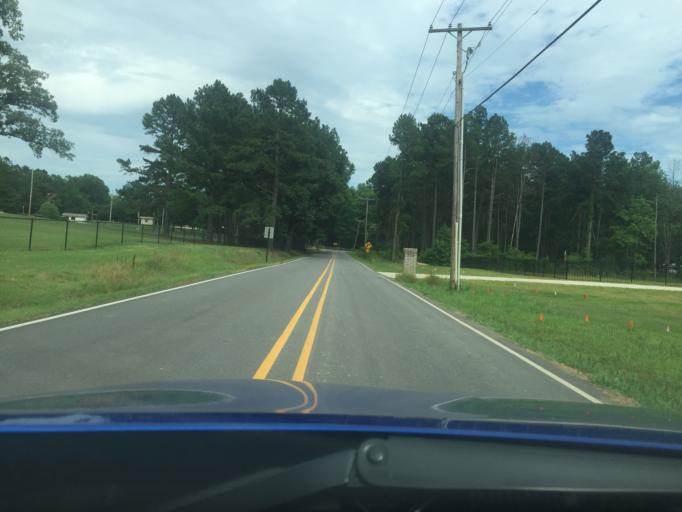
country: US
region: Arkansas
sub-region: Pulaski County
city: Maumelle
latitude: 34.8301
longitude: -92.4381
